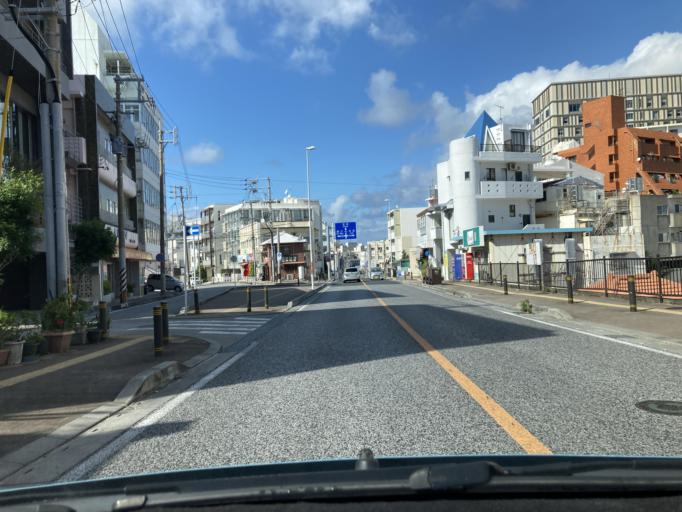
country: JP
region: Okinawa
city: Naha-shi
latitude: 26.2132
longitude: 127.6852
